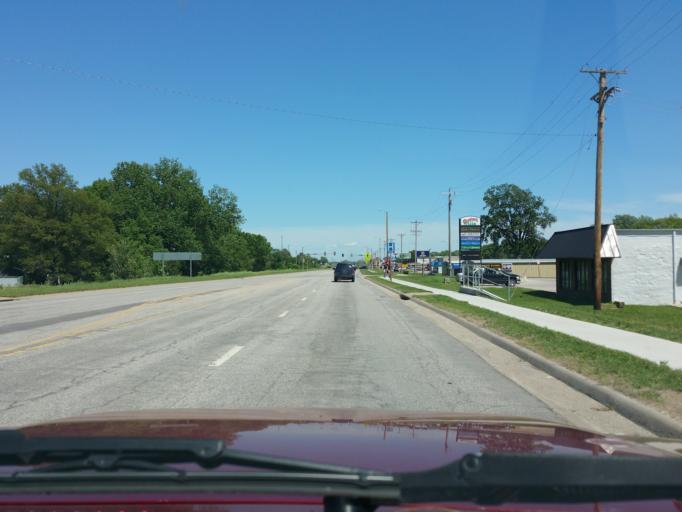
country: US
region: Kansas
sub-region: Pottawatomie County
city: Wamego
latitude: 39.2101
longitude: -96.3143
